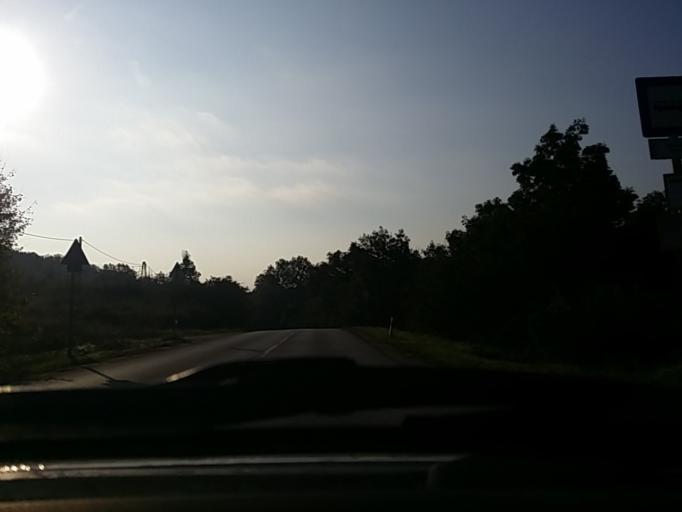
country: HU
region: Pest
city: Szentendre
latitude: 47.6891
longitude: 19.0374
